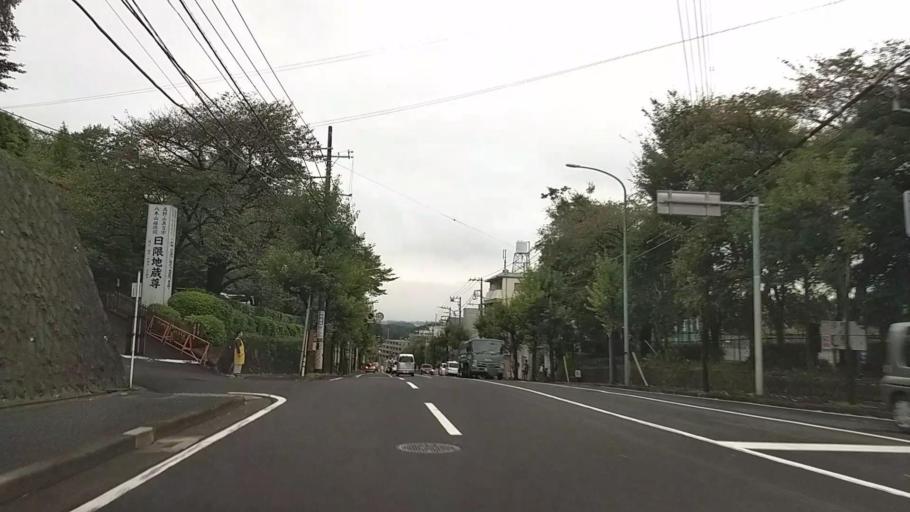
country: JP
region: Kanagawa
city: Kamakura
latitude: 35.3989
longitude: 139.5600
